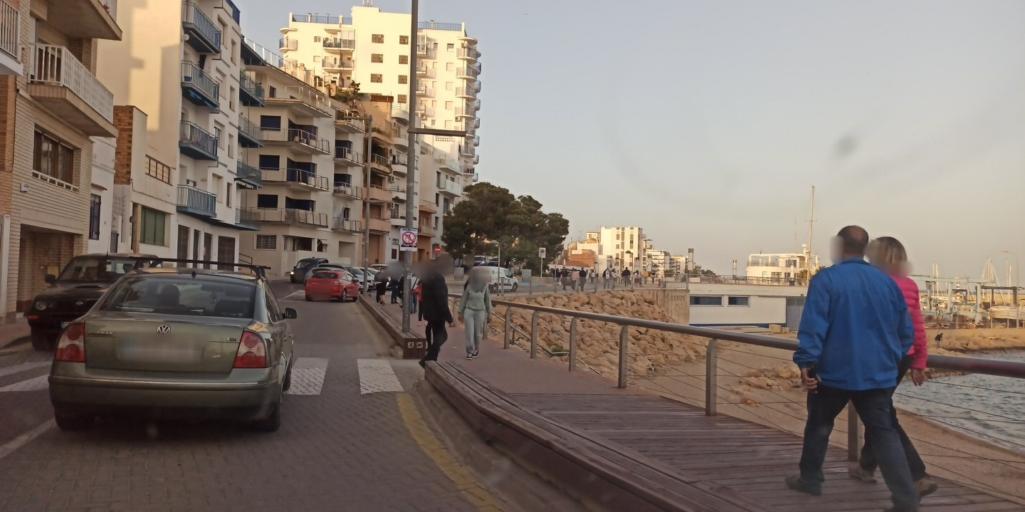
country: ES
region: Catalonia
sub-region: Provincia de Tarragona
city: L'Ampolla
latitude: 40.8100
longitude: 0.7062
